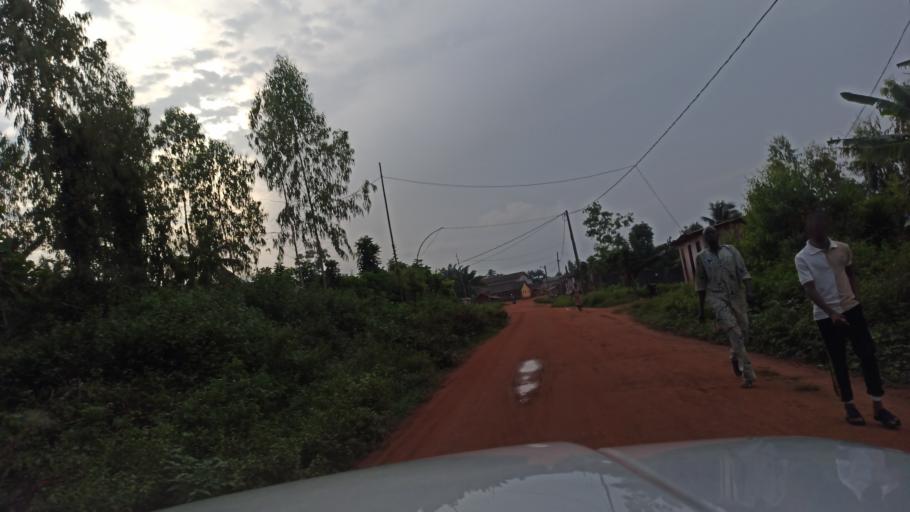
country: BJ
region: Queme
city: Porto-Novo
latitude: 6.5031
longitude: 2.6975
